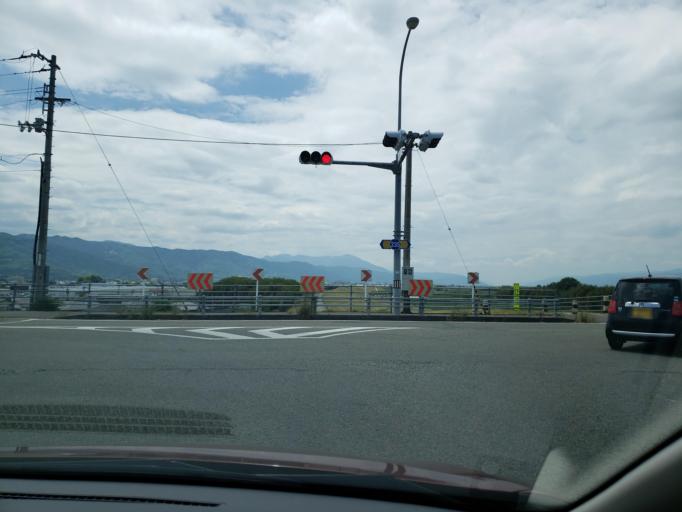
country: JP
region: Tokushima
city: Kamojimacho-jogejima
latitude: 34.0868
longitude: 134.3885
